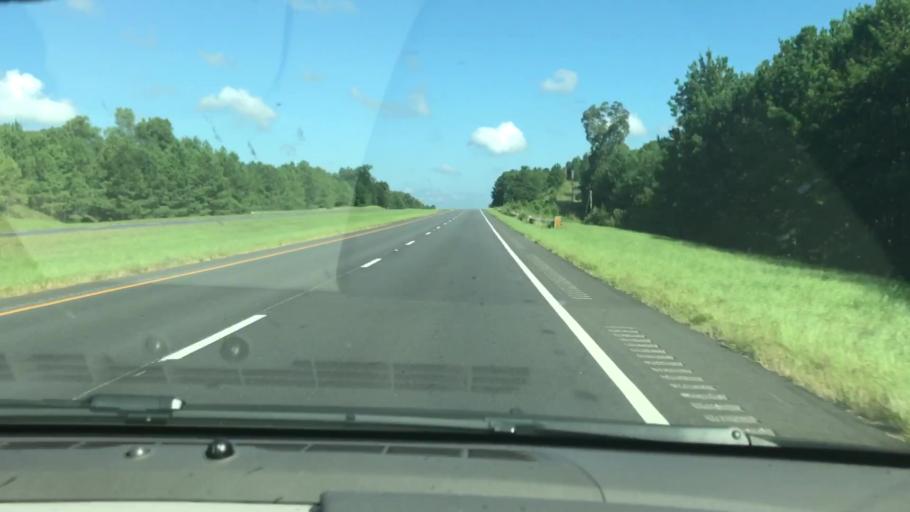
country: US
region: Alabama
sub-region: Barbour County
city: Eufaula
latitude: 32.0437
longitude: -85.1294
